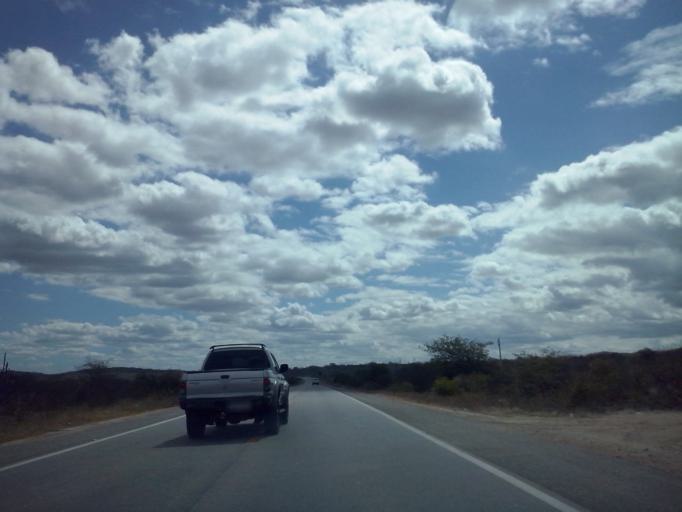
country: BR
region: Paraiba
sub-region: Soledade
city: Soledade
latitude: -7.0451
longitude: -36.3937
